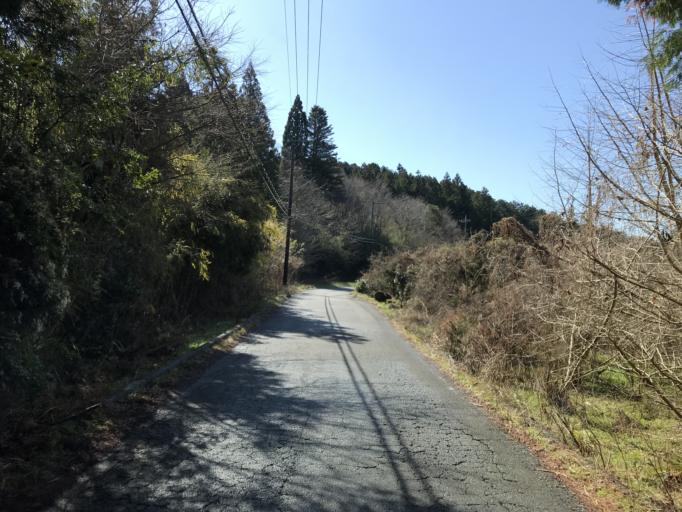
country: JP
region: Shizuoka
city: Fujinomiya
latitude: 35.2472
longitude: 138.6615
